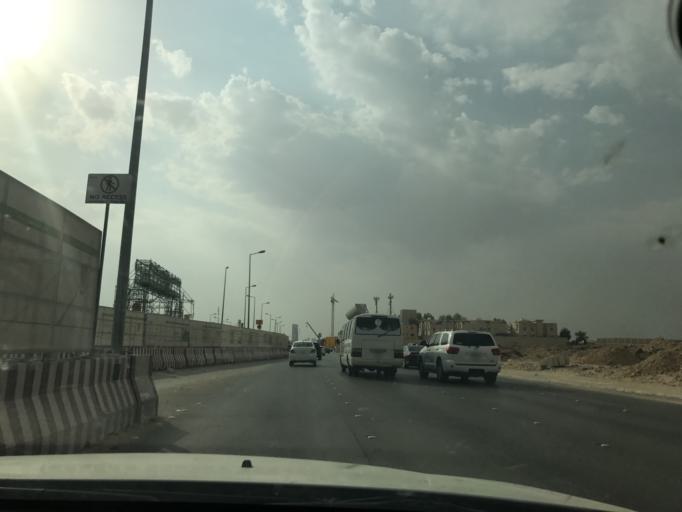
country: SA
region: Ar Riyad
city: Riyadh
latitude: 24.7105
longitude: 46.7058
